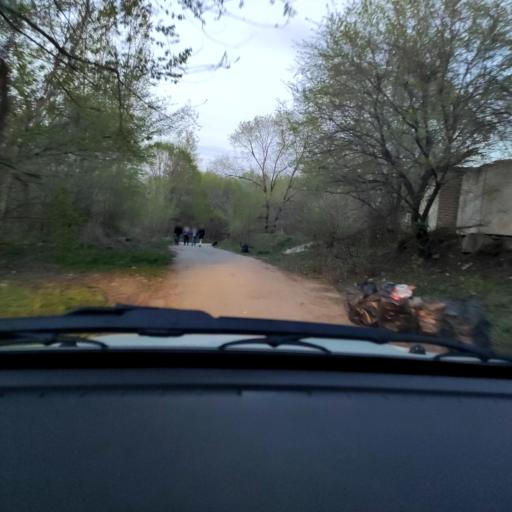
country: RU
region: Voronezj
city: Pridonskoy
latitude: 51.6592
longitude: 39.1027
